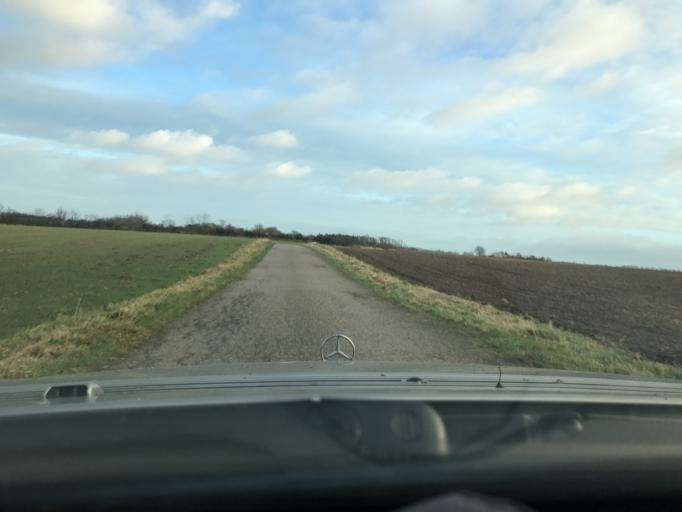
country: DK
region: South Denmark
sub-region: Sonderborg Kommune
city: Nordborg
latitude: 55.0512
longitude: 9.6700
